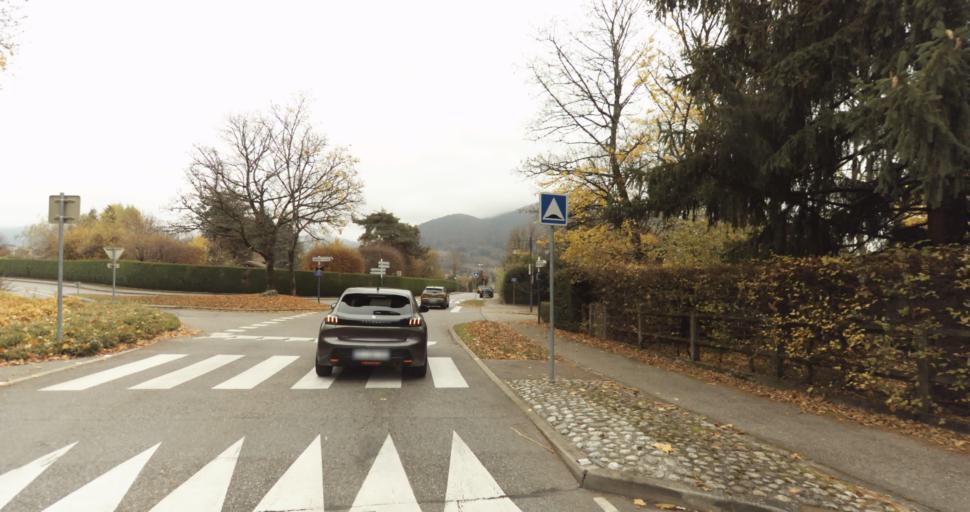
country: FR
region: Rhone-Alpes
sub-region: Departement de la Haute-Savoie
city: Annecy-le-Vieux
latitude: 45.9212
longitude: 6.1425
